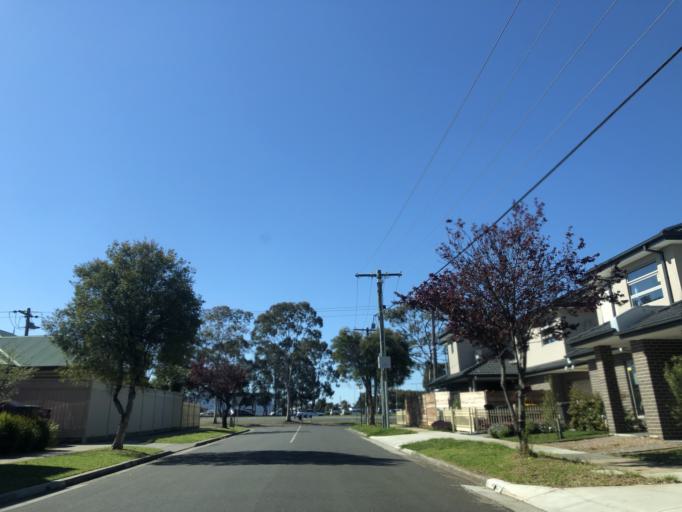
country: AU
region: Victoria
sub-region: Monash
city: Clayton
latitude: -37.9172
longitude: 145.1412
